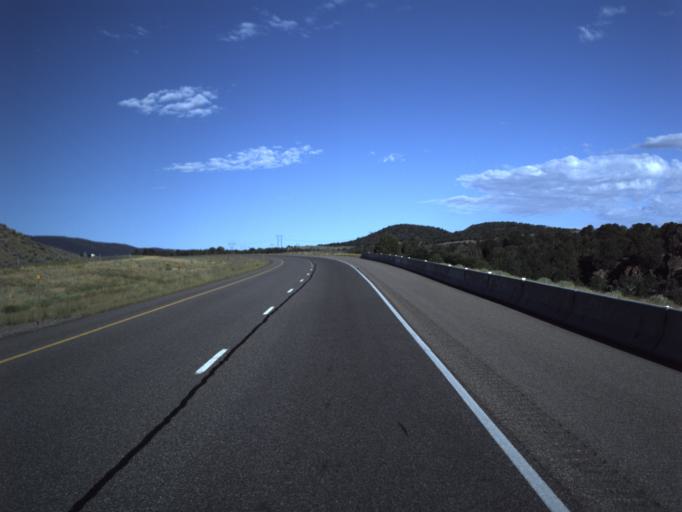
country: US
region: Utah
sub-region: Sevier County
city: Monroe
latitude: 38.5507
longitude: -112.3883
